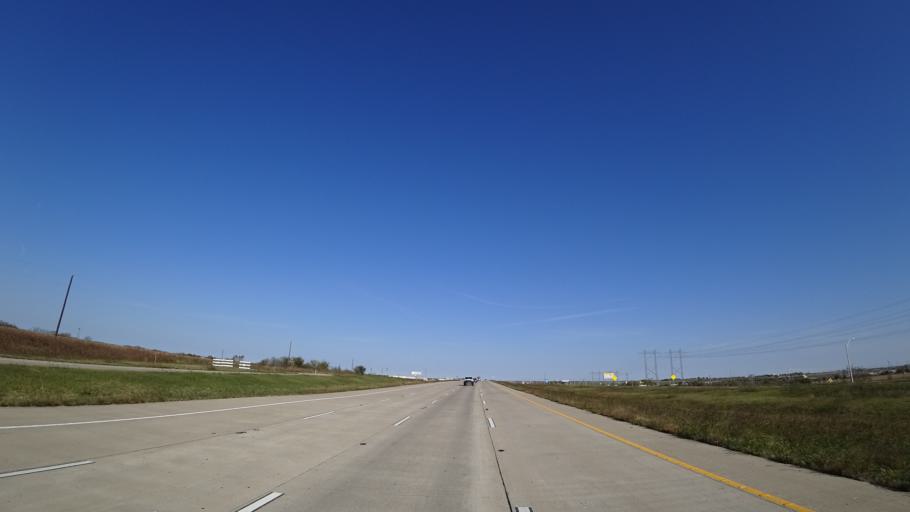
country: US
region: Texas
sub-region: Travis County
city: Pflugerville
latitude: 30.4016
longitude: -97.5826
